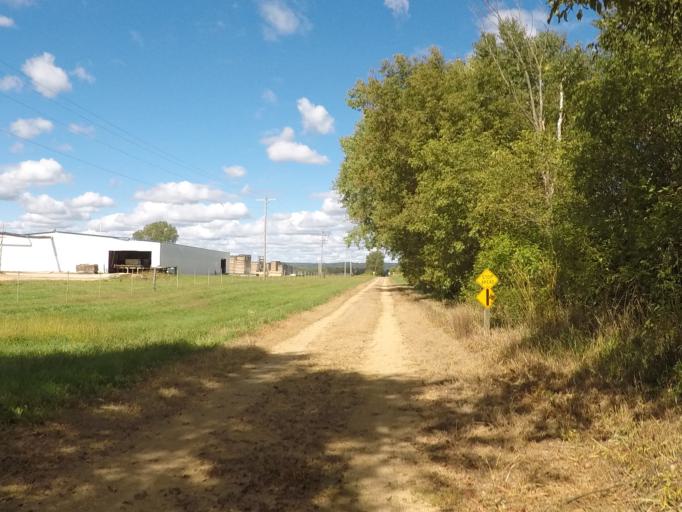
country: US
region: Wisconsin
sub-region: Richland County
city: Richland Center
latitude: 43.2913
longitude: -90.3259
